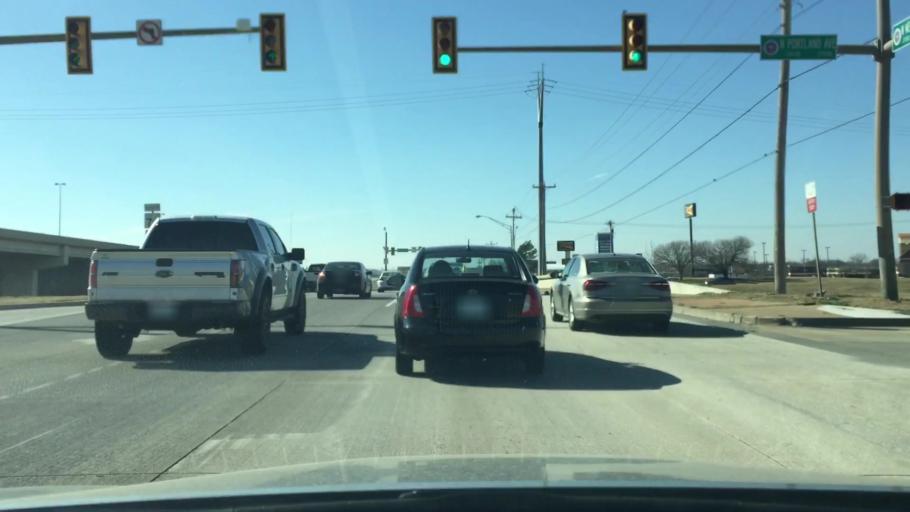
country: US
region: Oklahoma
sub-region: Oklahoma County
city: The Village
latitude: 35.6101
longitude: -97.5843
